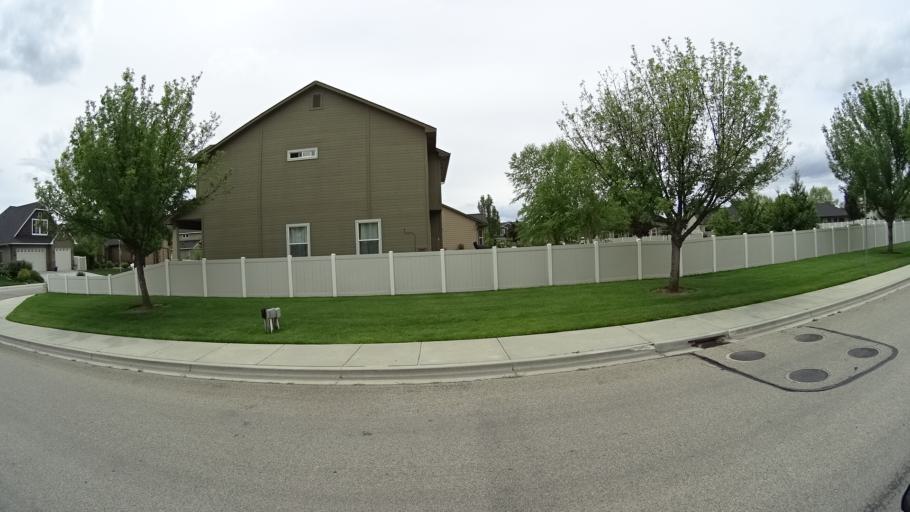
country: US
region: Idaho
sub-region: Ada County
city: Meridian
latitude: 43.6449
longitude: -116.4018
